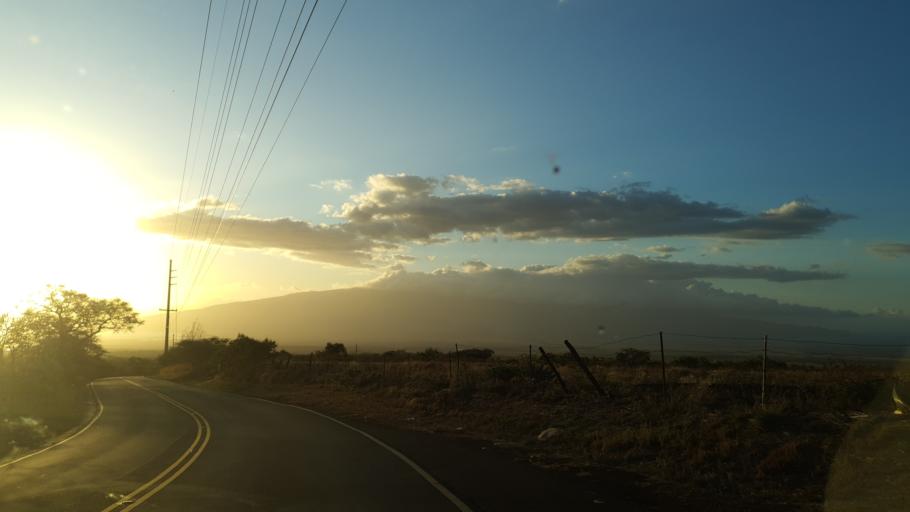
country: US
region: Hawaii
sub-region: Maui County
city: Pukalani
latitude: 20.7927
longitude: -156.3602
